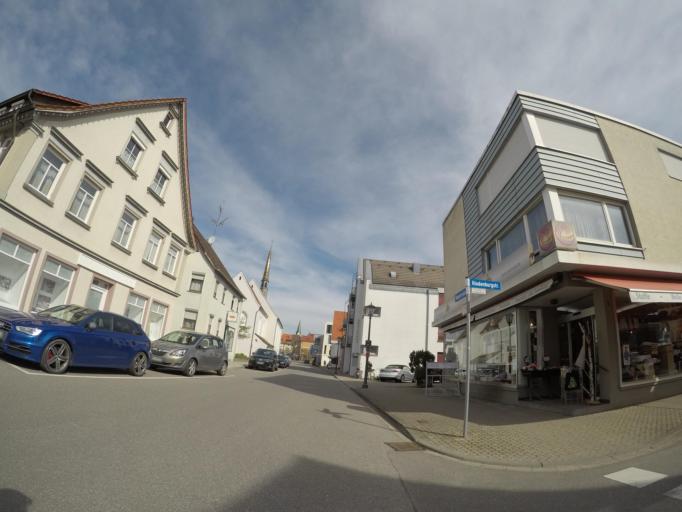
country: DE
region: Baden-Wuerttemberg
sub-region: Tuebingen Region
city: Saulgau
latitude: 48.0143
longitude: 9.5027
